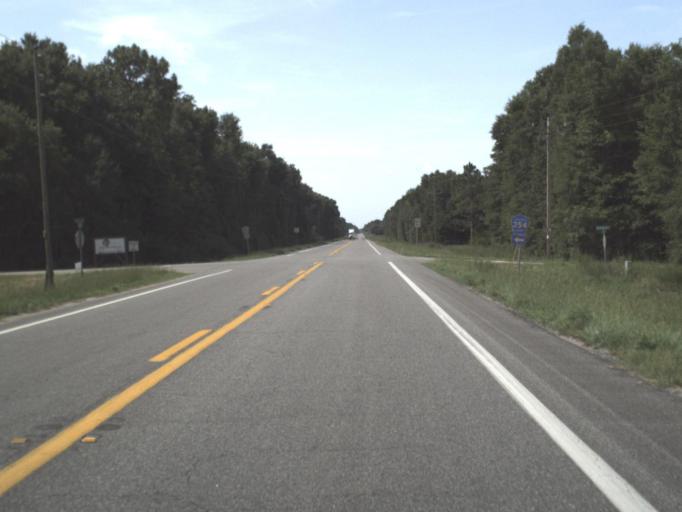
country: US
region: Florida
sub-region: Lafayette County
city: Mayo
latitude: 30.0933
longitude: -83.1723
